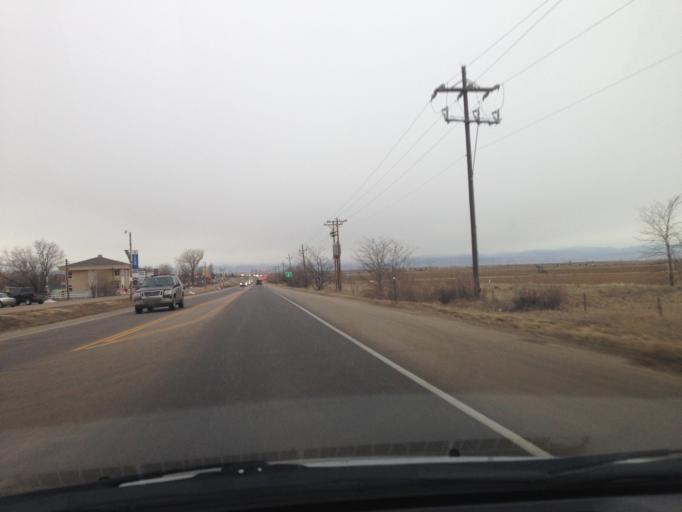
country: US
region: Colorado
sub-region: Weld County
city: Dacono
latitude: 40.0879
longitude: -104.9334
